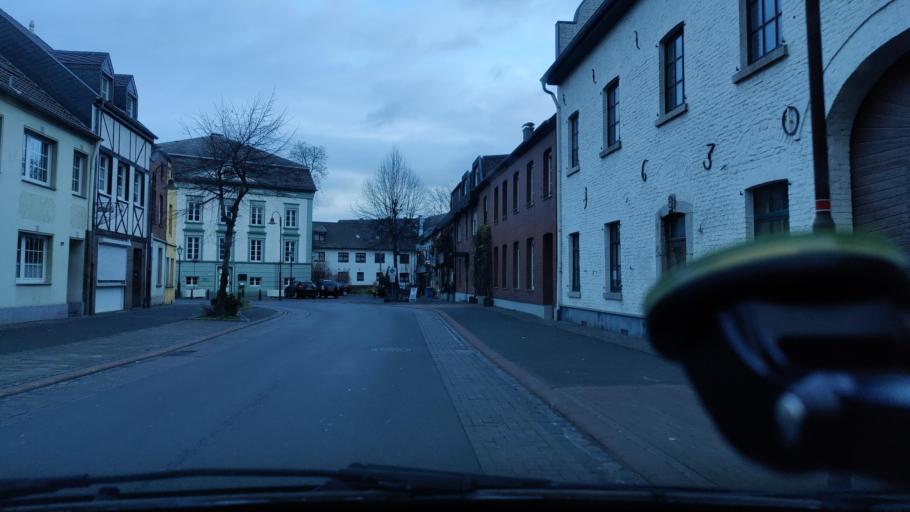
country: DE
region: North Rhine-Westphalia
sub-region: Regierungsbezirk Koln
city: Aldenhoven
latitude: 50.8947
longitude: 6.2865
